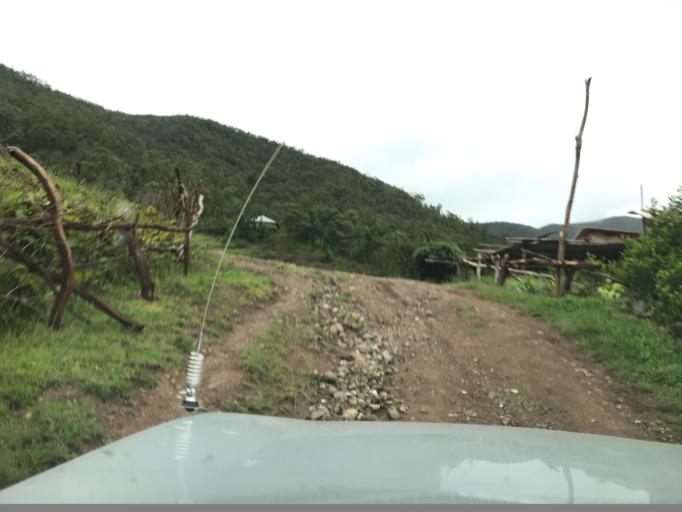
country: TL
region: Ainaro
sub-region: Ainaro
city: Ainaro
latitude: -8.8692
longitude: 125.5518
